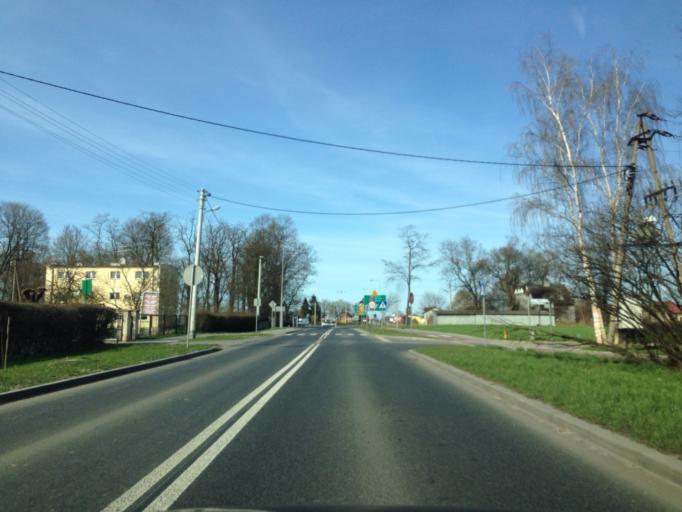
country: PL
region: Lodz Voivodeship
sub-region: Powiat poddebicki
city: Wartkowice
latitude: 51.9713
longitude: 19.0175
